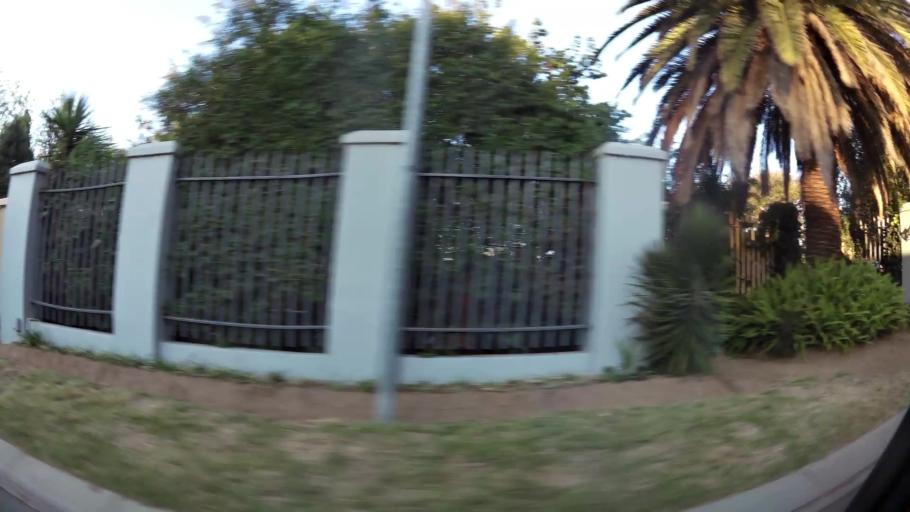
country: ZA
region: Gauteng
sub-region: City of Johannesburg Metropolitan Municipality
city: Diepsloot
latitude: -26.0453
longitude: 27.9770
